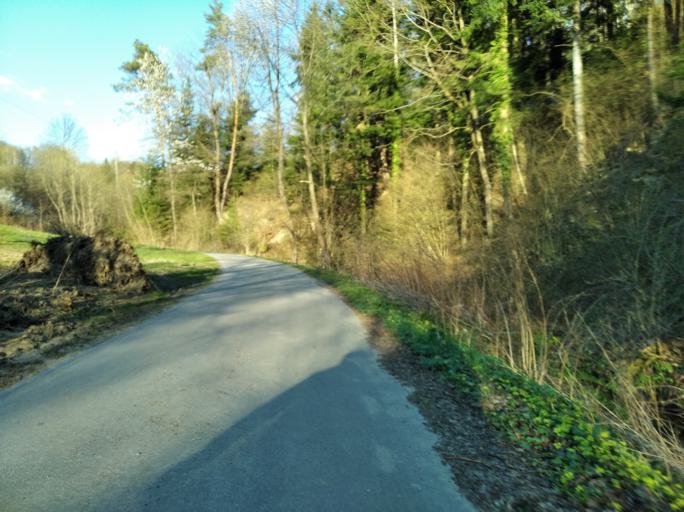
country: PL
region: Subcarpathian Voivodeship
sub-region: Powiat strzyzowski
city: Strzyzow
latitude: 49.8764
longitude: 21.8315
